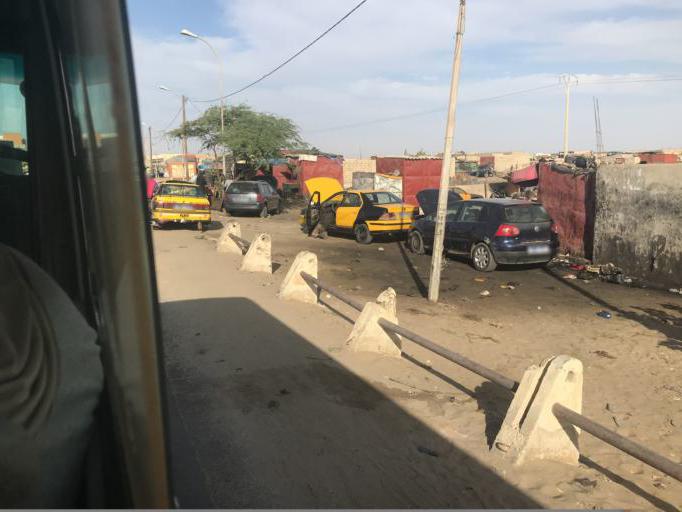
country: SN
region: Saint-Louis
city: Saint-Louis
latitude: 15.9886
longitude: -16.4876
